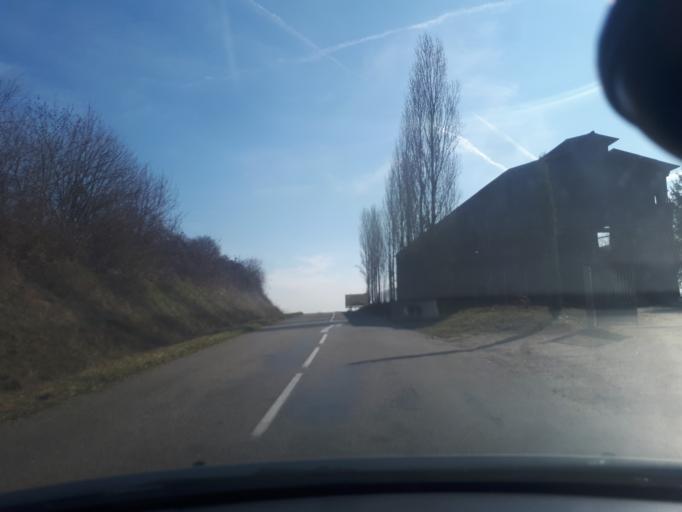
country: FR
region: Rhone-Alpes
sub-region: Departement de l'Isere
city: Sermerieu
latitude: 45.6689
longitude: 5.4173
